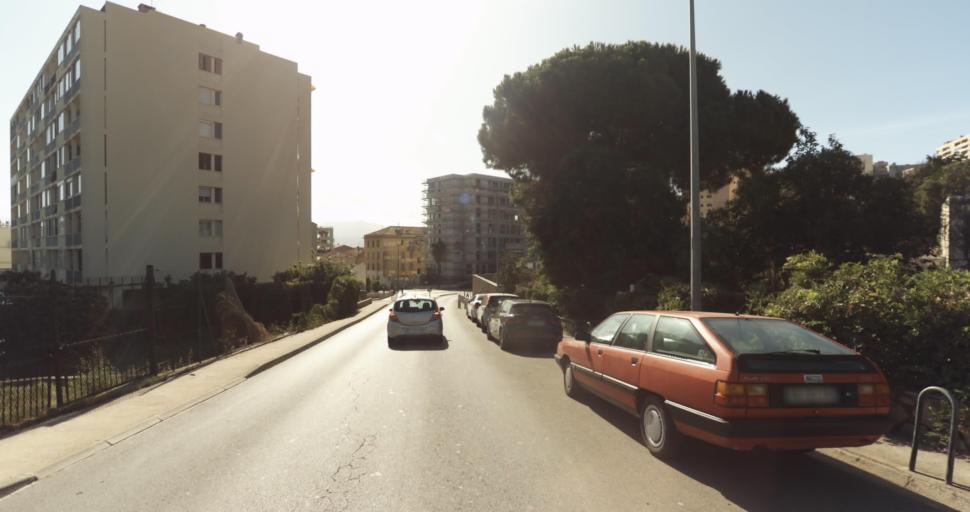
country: FR
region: Corsica
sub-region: Departement de la Corse-du-Sud
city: Ajaccio
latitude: 41.9273
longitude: 8.7341
